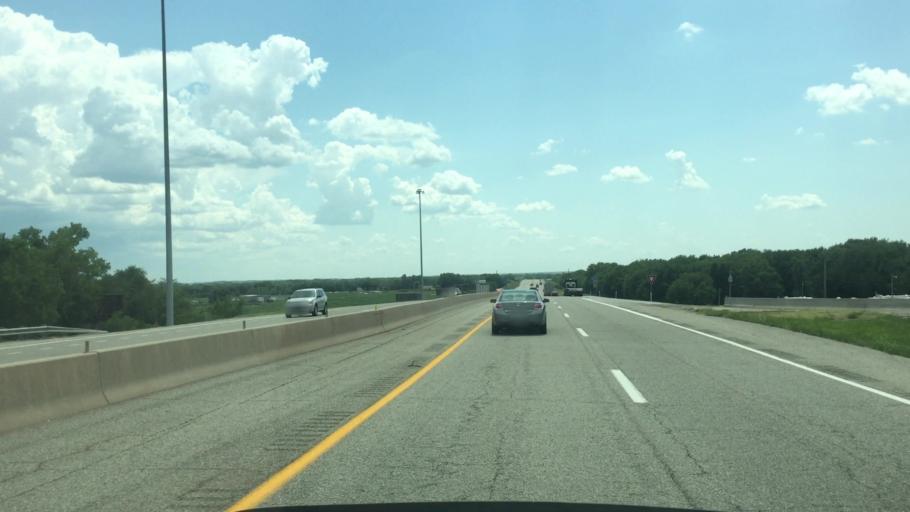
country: US
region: Kansas
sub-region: Lyon County
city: Emporia
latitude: 38.4119
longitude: -96.2398
